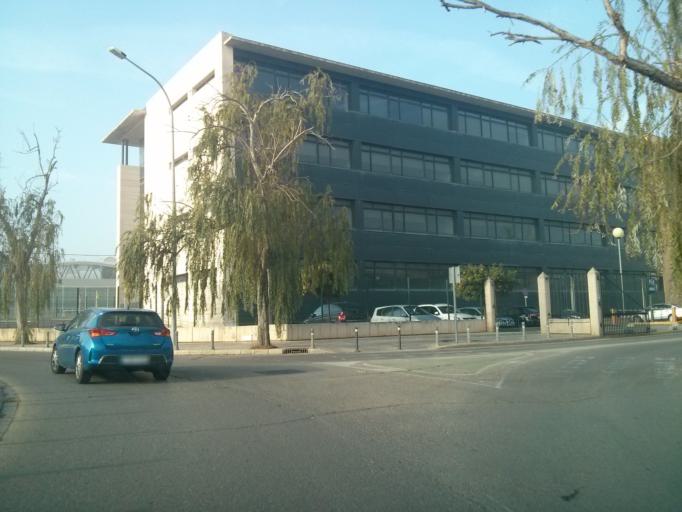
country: ES
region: Valencia
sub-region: Provincia de Valencia
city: Alboraya
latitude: 39.4830
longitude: -0.3405
